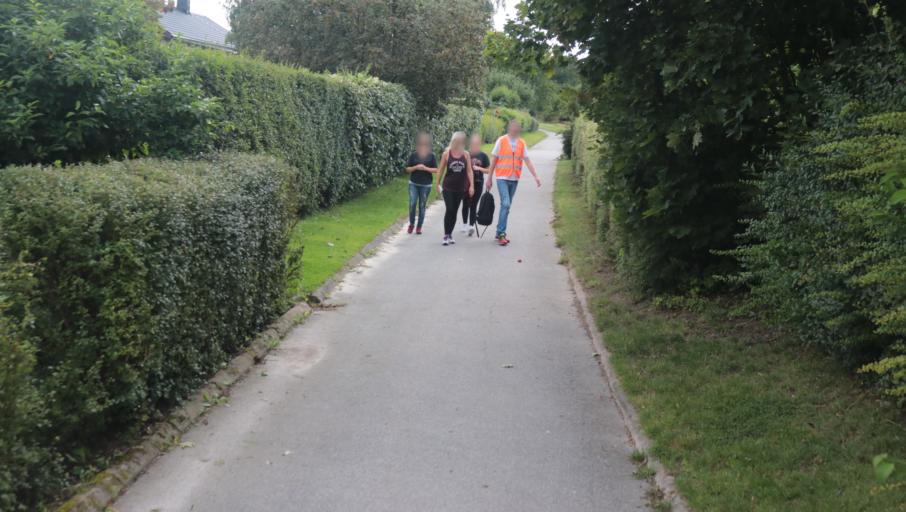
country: SE
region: Blekinge
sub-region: Karlshamns Kommun
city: Karlshamn
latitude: 56.2097
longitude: 14.8468
